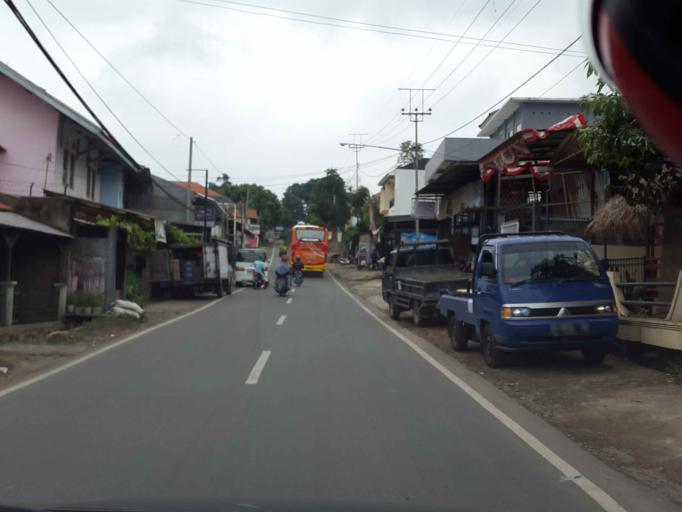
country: ID
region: West Java
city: Lembang
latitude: -6.8052
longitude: 107.5934
